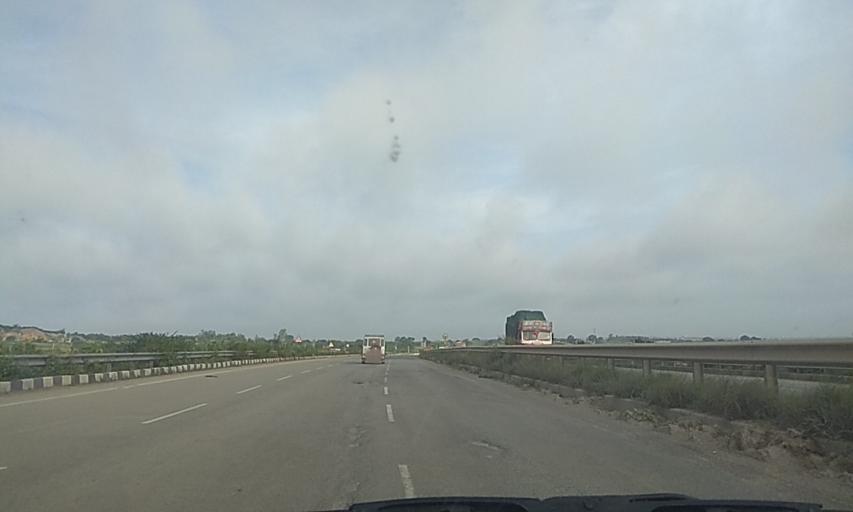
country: IN
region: Karnataka
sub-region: Haveri
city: Haveri
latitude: 14.7631
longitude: 75.4324
